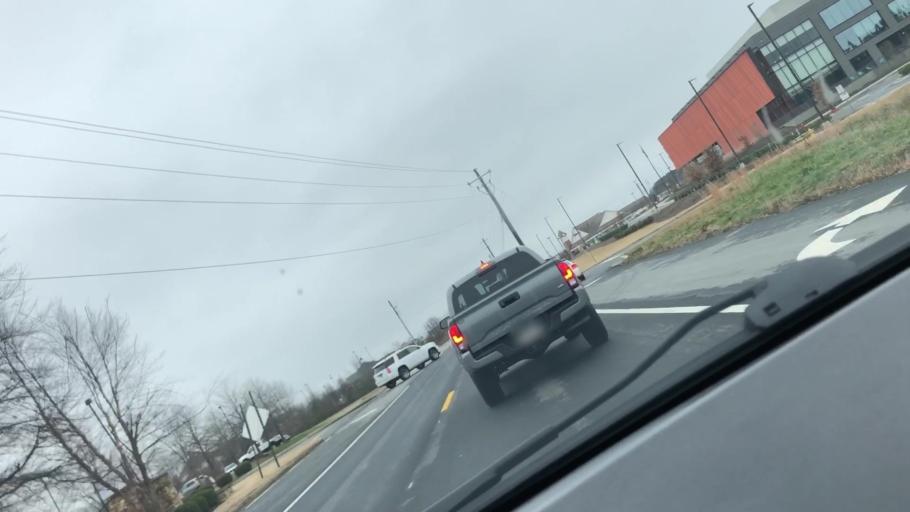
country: US
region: Georgia
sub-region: Bartow County
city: Cartersville
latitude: 34.1470
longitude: -84.8243
